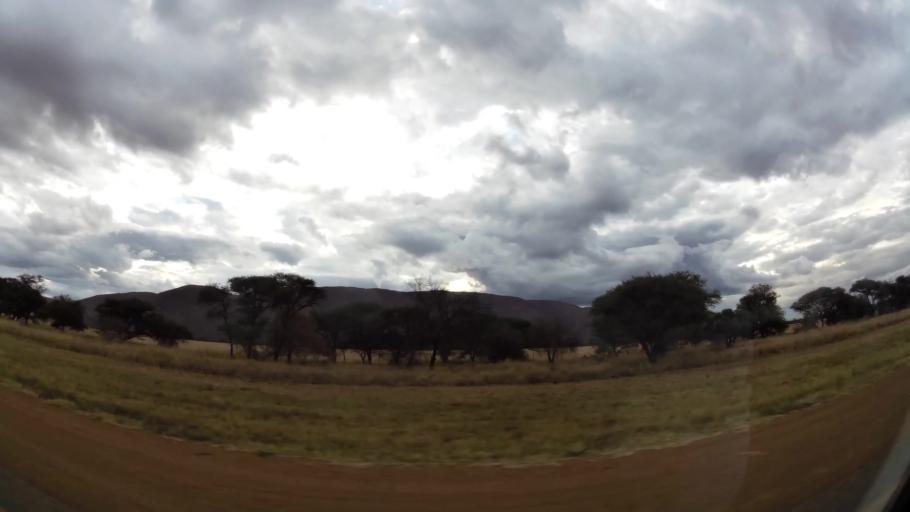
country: ZA
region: Limpopo
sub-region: Waterberg District Municipality
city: Mokopane
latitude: -24.2489
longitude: 28.9912
